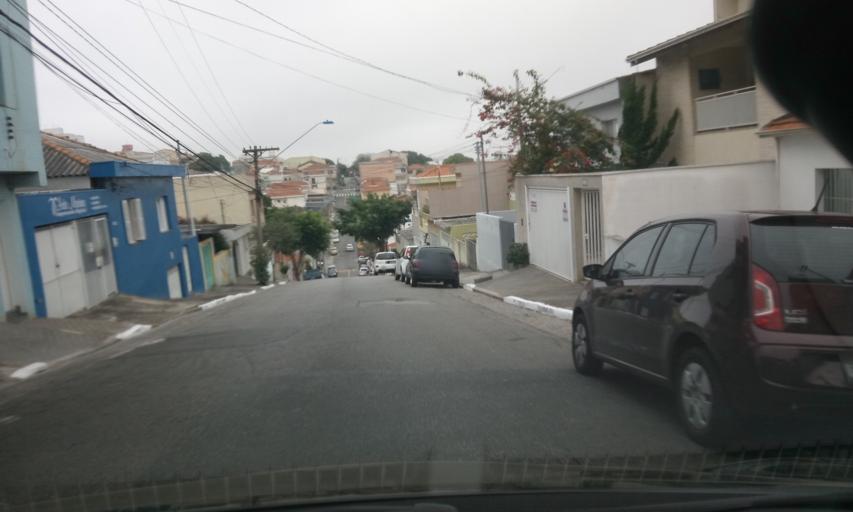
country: BR
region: Sao Paulo
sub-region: Sao Caetano Do Sul
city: Sao Caetano do Sul
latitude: -23.6246
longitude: -46.5733
